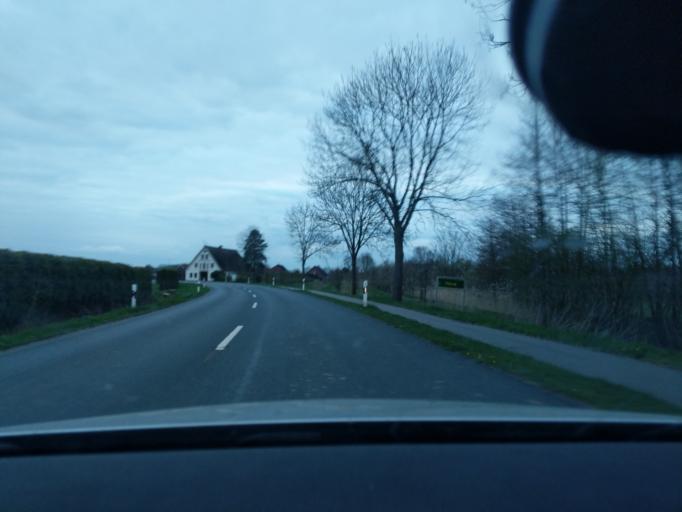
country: DE
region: Lower Saxony
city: Jork
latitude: 53.5253
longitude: 9.7439
